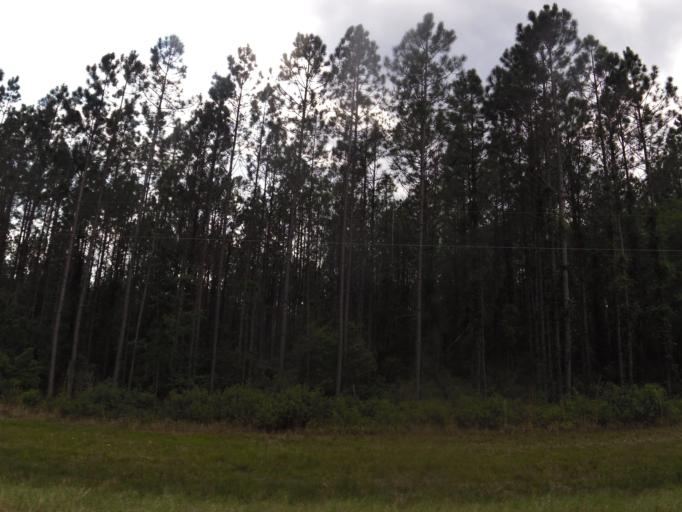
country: US
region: Georgia
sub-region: Charlton County
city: Folkston
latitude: 30.8679
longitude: -82.0138
